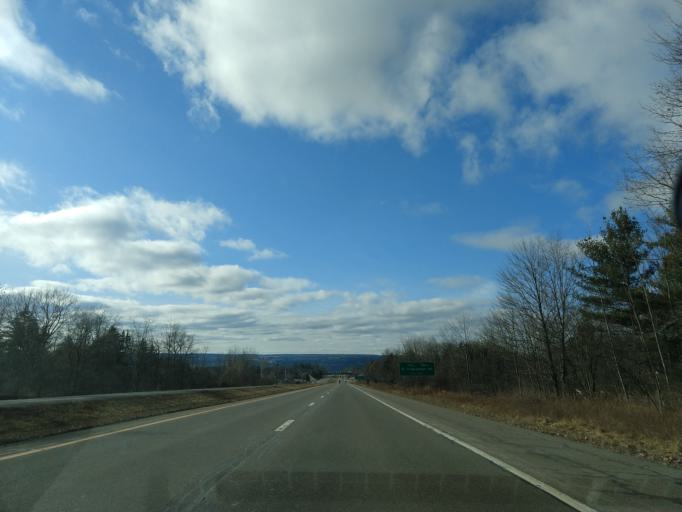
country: US
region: New York
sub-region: Tompkins County
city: Lansing
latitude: 42.4820
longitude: -76.4736
